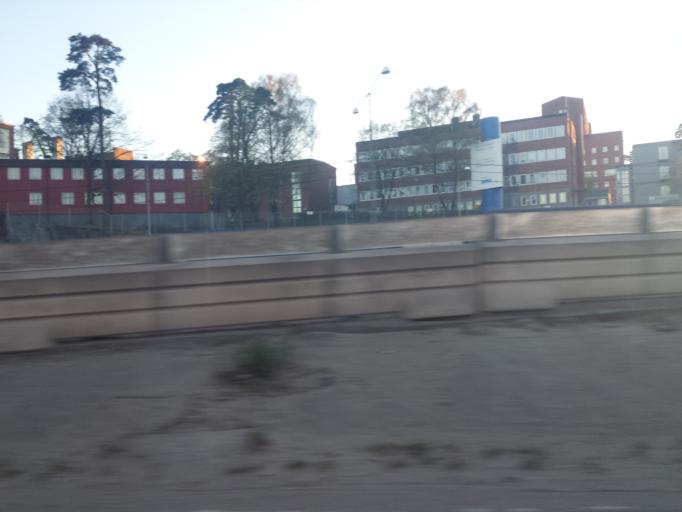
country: SE
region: Stockholm
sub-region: Norrtalje Kommun
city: Bergshamra
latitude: 59.3534
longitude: 18.0392
